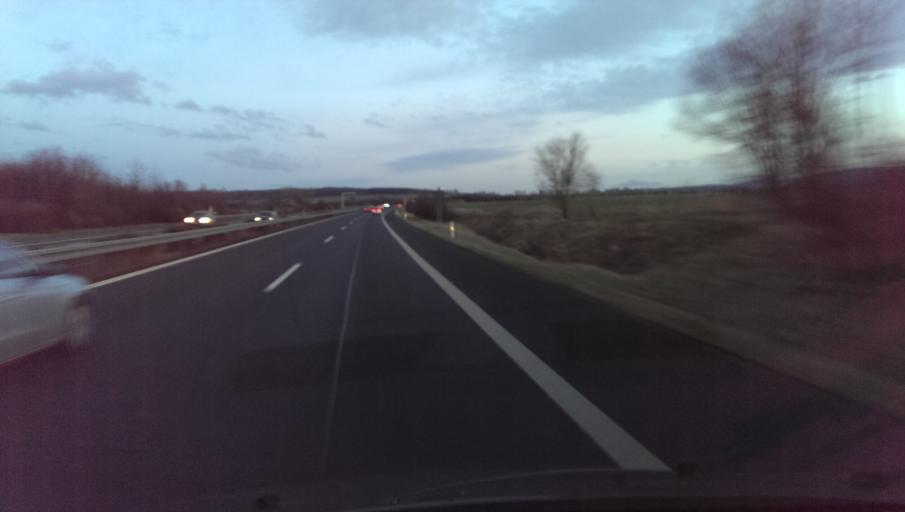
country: DE
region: Saxony-Anhalt
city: Stapelburg
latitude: 51.9337
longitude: 10.6391
